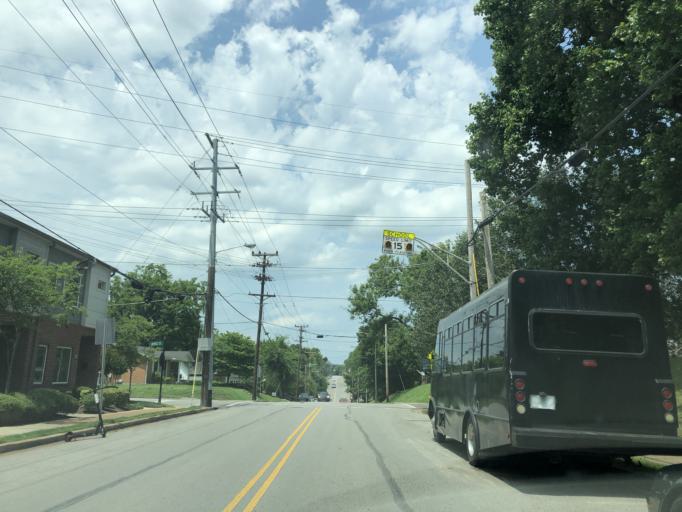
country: US
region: Tennessee
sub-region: Davidson County
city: Nashville
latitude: 36.1777
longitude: -86.7554
